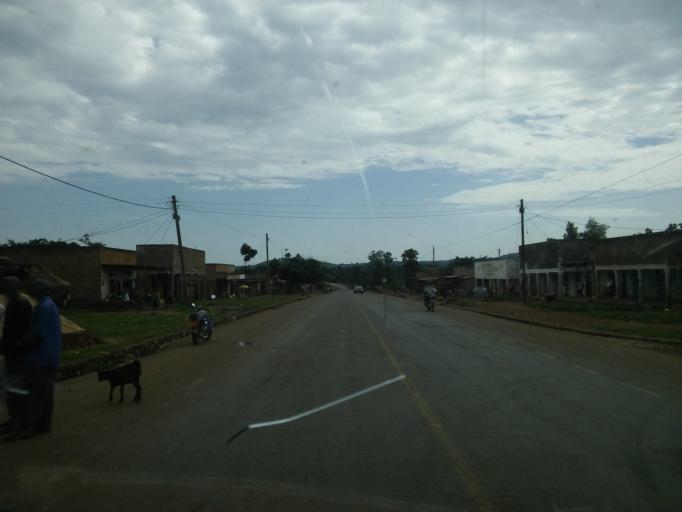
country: UG
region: Eastern Region
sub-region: Mbale District
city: Mbale
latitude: 1.1451
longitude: 34.1646
